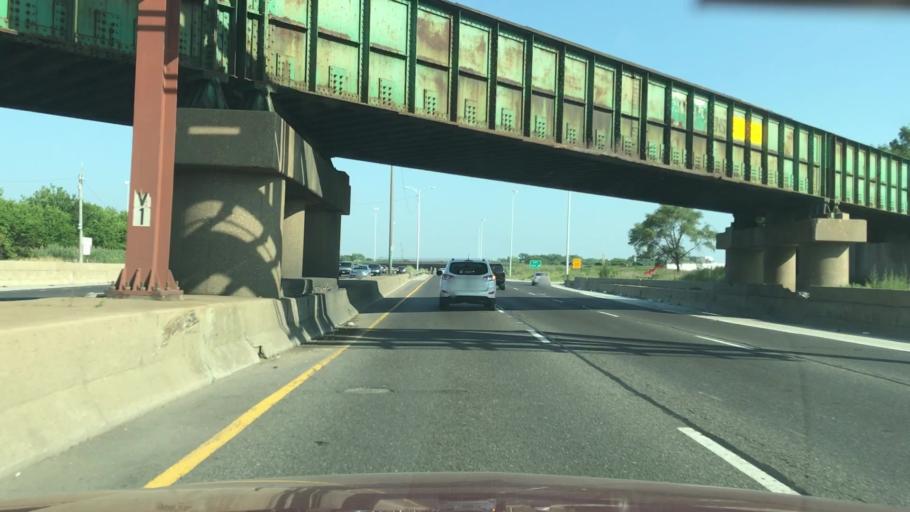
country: US
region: Illinois
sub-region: Cook County
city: Dolton
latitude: 41.6636
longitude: -87.5919
